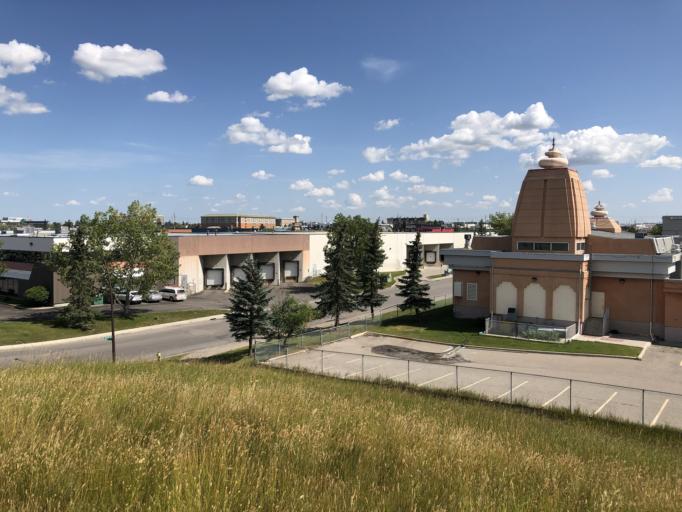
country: CA
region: Alberta
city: Calgary
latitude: 51.0738
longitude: -114.0091
